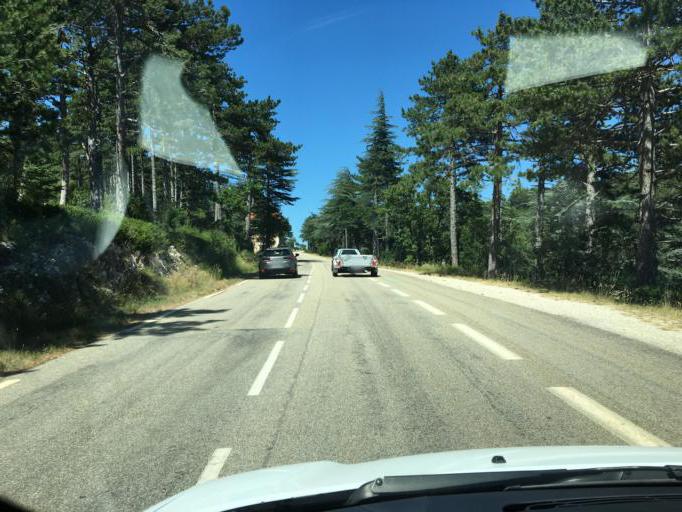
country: FR
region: Provence-Alpes-Cote d'Azur
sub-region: Departement du Vaucluse
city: Bedoin
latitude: 44.1668
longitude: 5.1946
